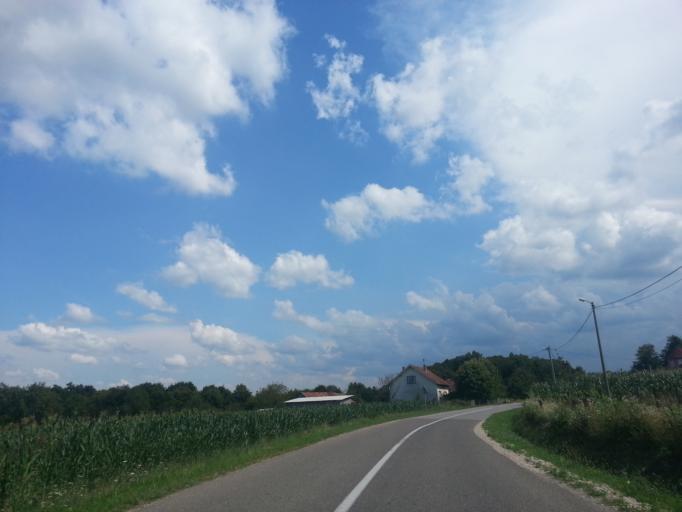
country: BA
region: Brcko
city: Brcko
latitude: 44.8016
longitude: 18.8414
